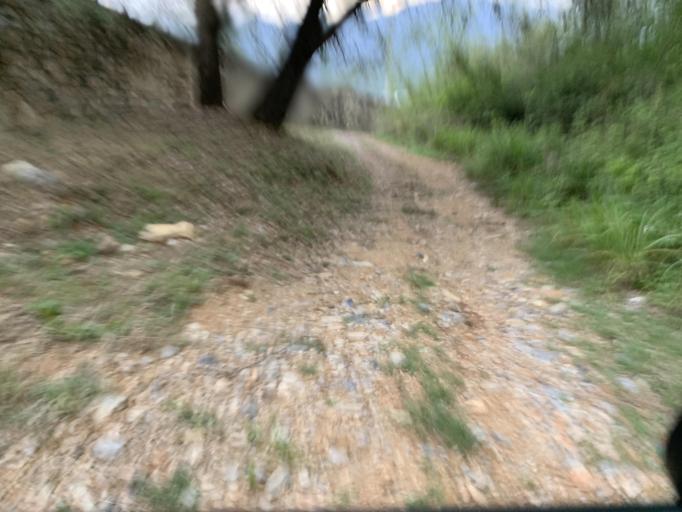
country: MX
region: Nuevo Leon
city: Santiago
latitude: 25.5061
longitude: -100.1772
